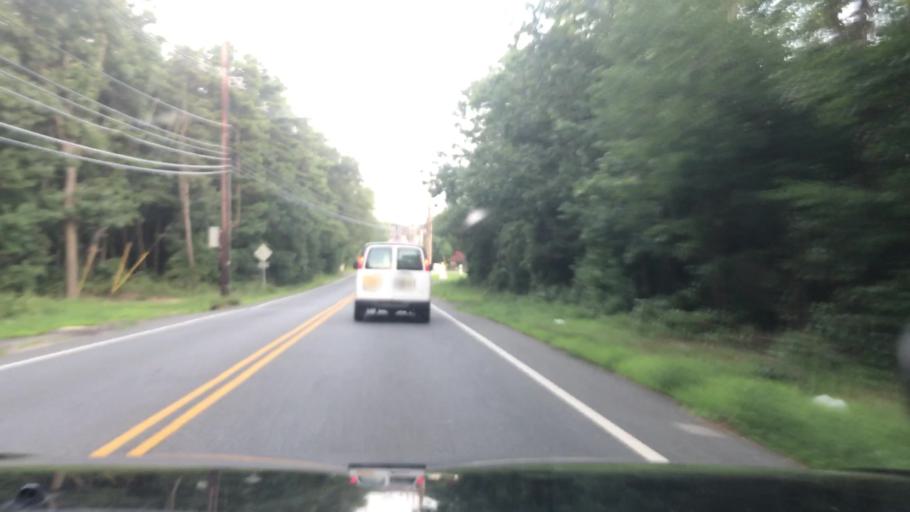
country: US
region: New Jersey
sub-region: Ocean County
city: Lakewood
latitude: 40.0581
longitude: -74.2264
